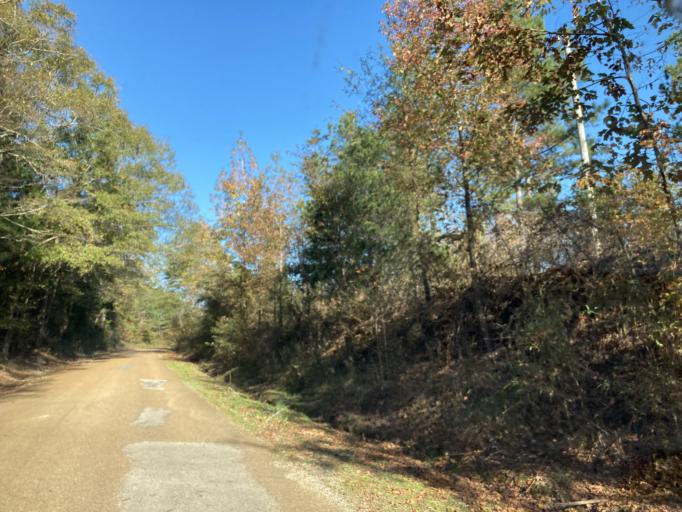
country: US
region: Mississippi
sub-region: Madison County
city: Kearney Park
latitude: 32.7355
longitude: -90.1986
